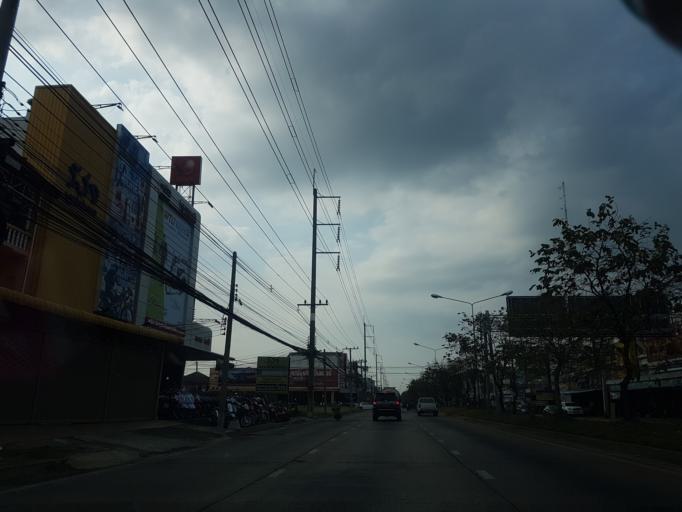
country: TH
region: Sara Buri
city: Phra Phutthabat
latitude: 14.7283
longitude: 100.7911
